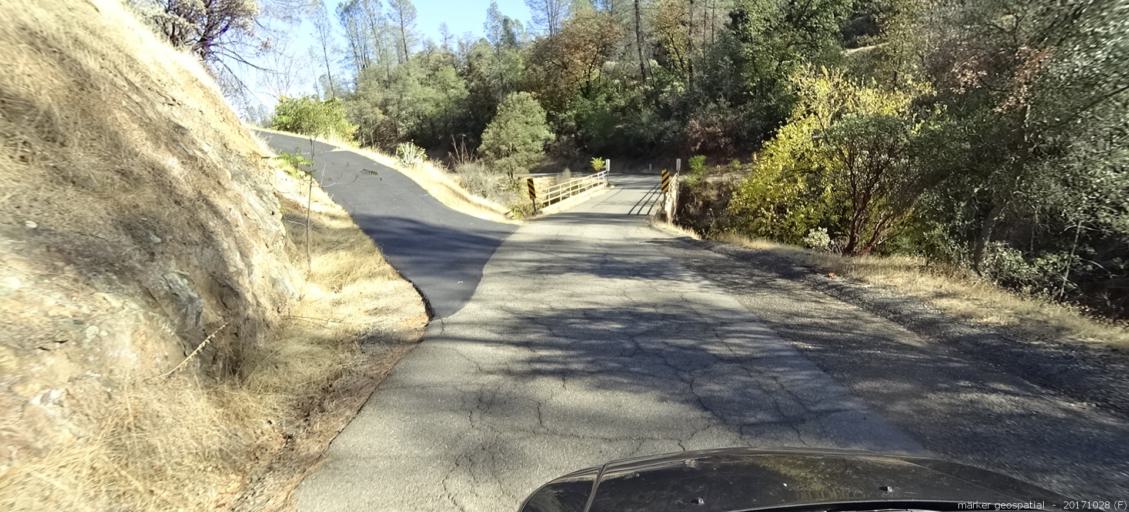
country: US
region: California
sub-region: Shasta County
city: Shasta
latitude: 40.5946
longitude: -122.4555
